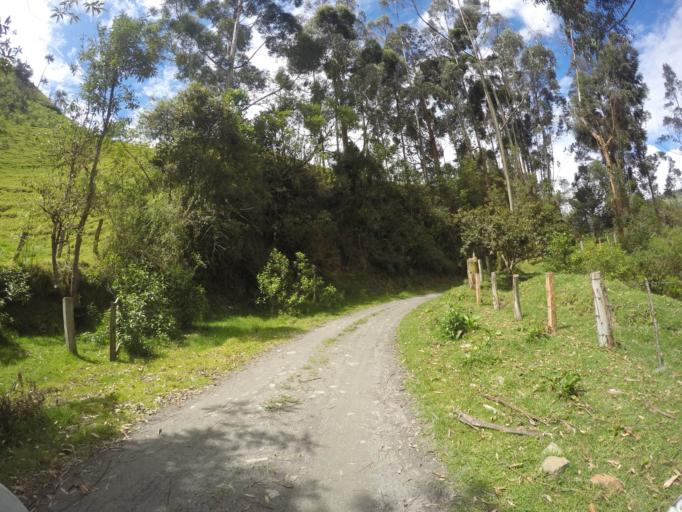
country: CO
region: Tolima
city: Cajamarca
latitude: 4.5296
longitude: -75.4551
